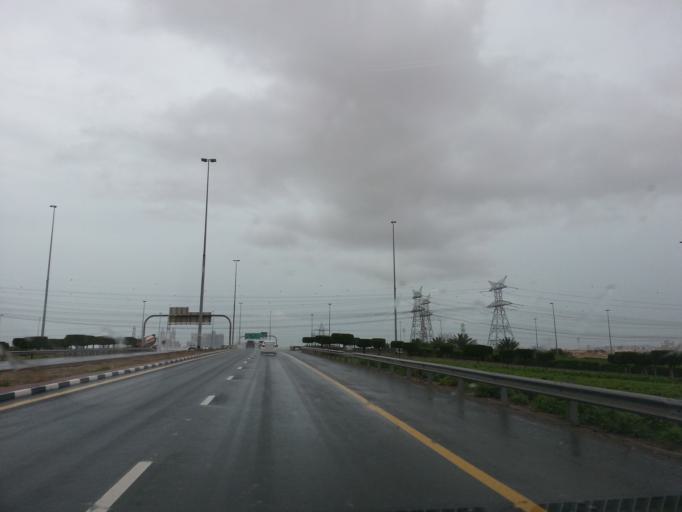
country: AE
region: Dubai
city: Dubai
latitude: 25.0753
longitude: 55.2125
